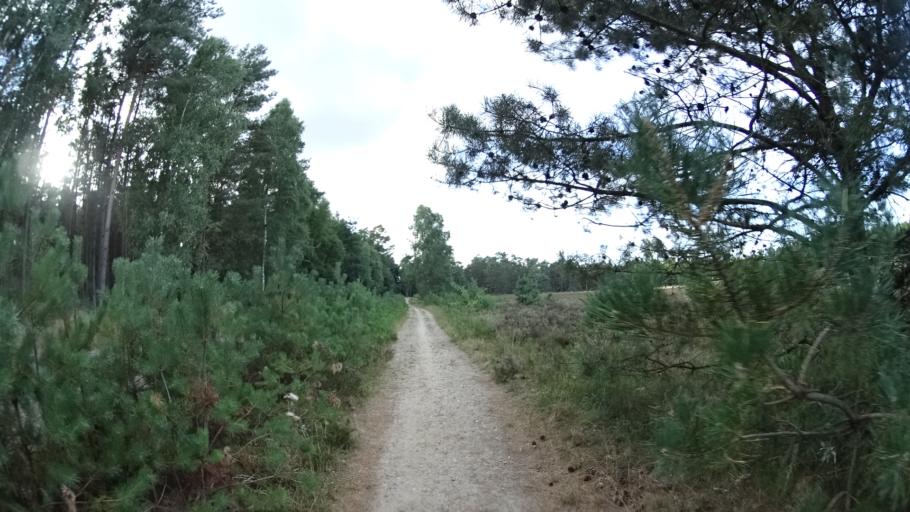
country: DE
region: Lower Saxony
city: Handeloh
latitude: 53.2284
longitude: 9.8729
